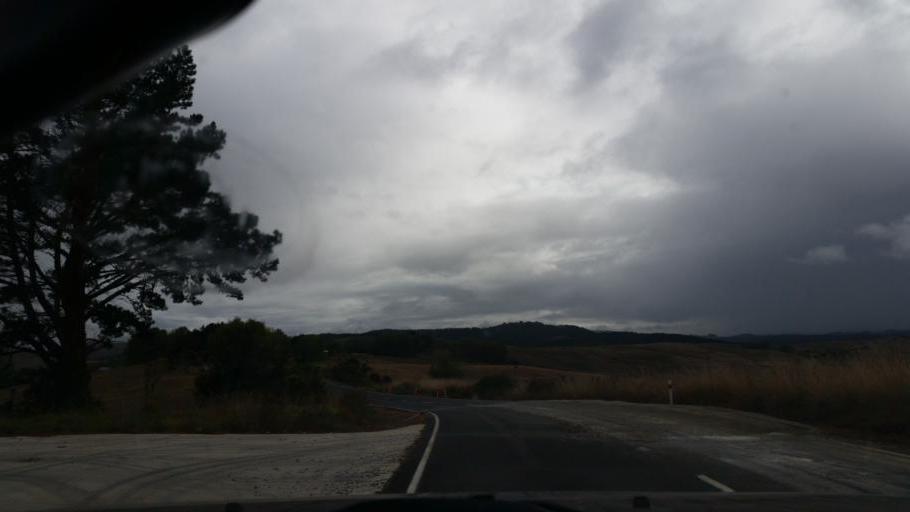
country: NZ
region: Auckland
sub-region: Auckland
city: Wellsford
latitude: -36.2233
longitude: 174.3784
